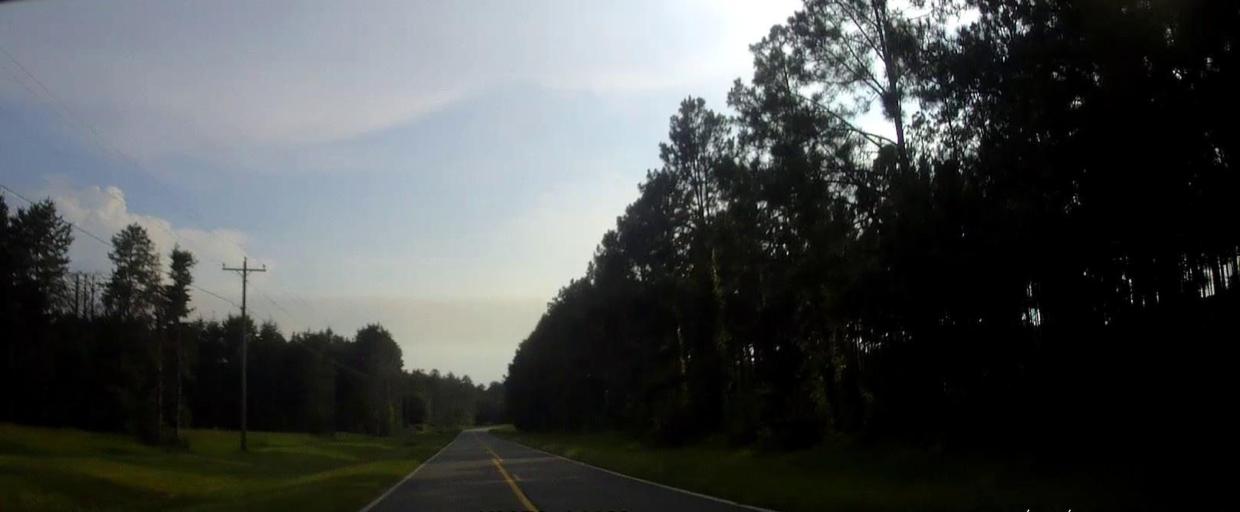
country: US
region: Georgia
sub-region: Laurens County
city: Dublin
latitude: 32.4814
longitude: -82.9498
